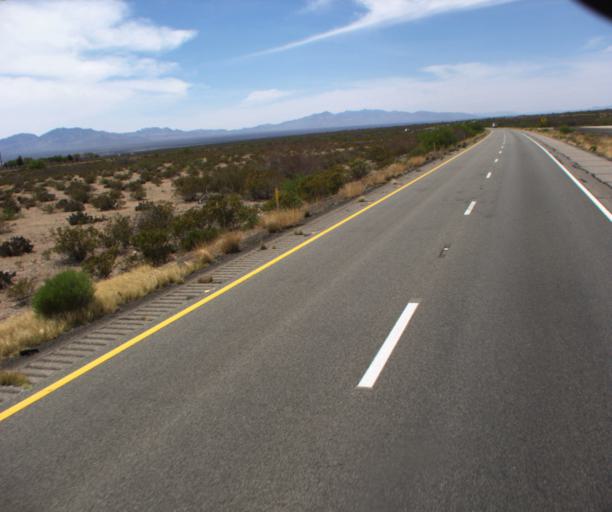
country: US
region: New Mexico
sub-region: Hidalgo County
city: Lordsburg
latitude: 32.2382
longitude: -109.0862
